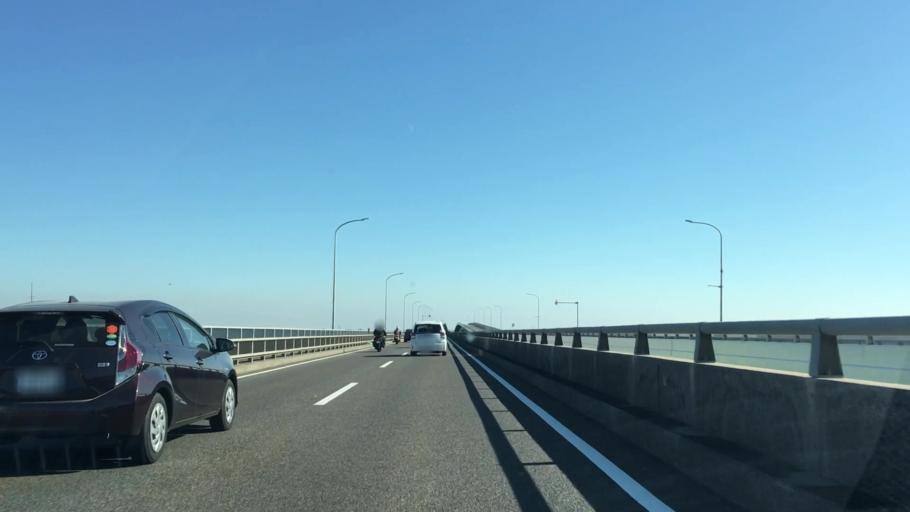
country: JP
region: Aichi
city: Tahara
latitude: 34.6936
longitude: 137.2983
